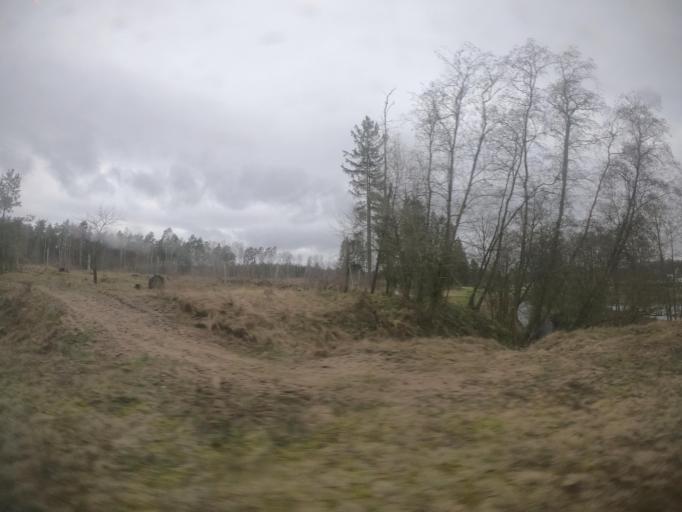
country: PL
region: West Pomeranian Voivodeship
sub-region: Powiat szczecinecki
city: Bialy Bor
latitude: 53.8317
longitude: 16.8744
